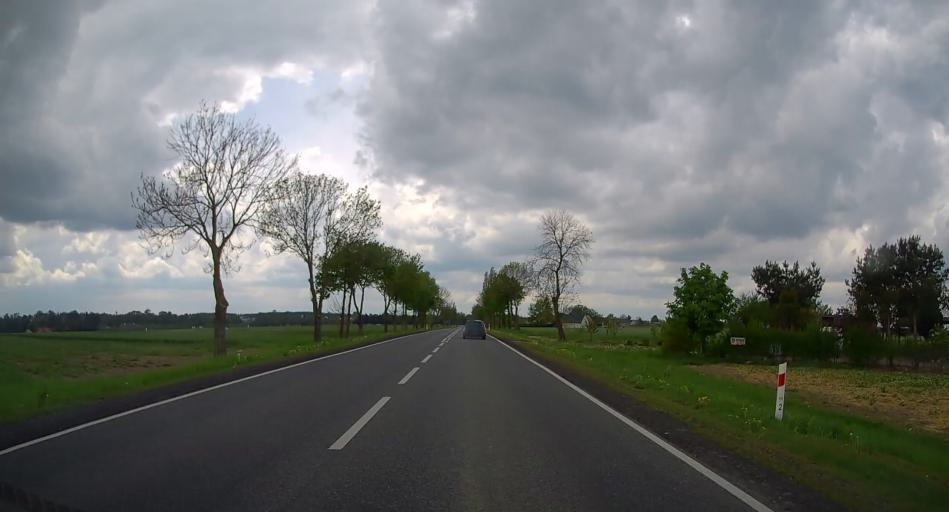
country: PL
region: Masovian Voivodeship
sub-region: Powiat plonski
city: Zaluski
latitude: 52.4368
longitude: 20.4760
